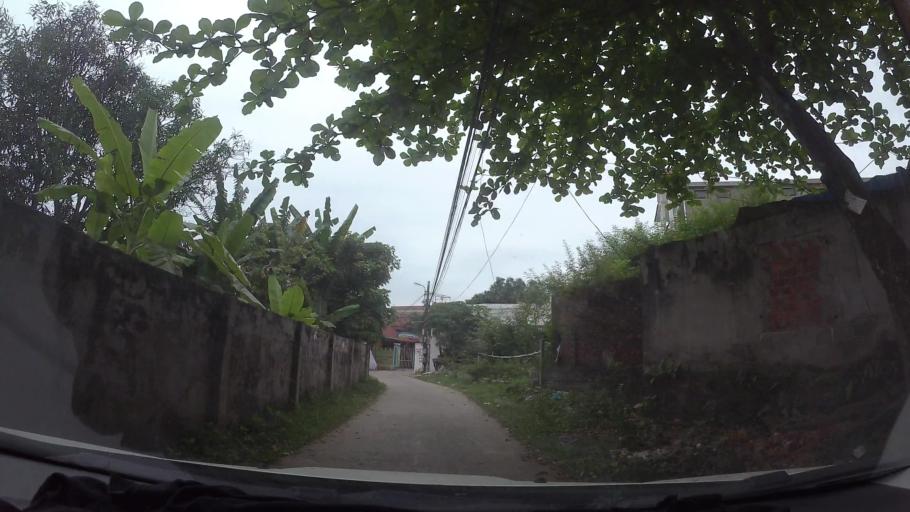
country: VN
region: Da Nang
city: Lien Chieu
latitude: 16.0673
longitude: 108.1444
